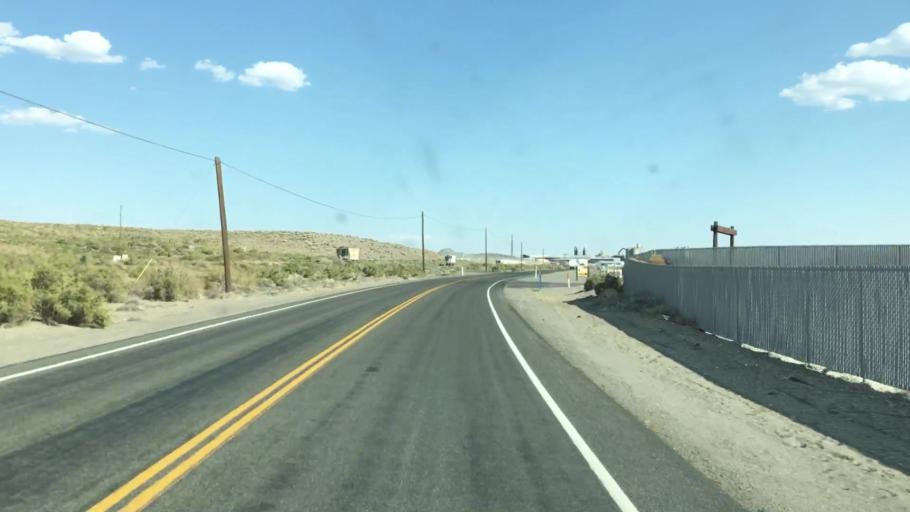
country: US
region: Nevada
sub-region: Lyon County
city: Fernley
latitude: 39.6298
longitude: -119.2769
